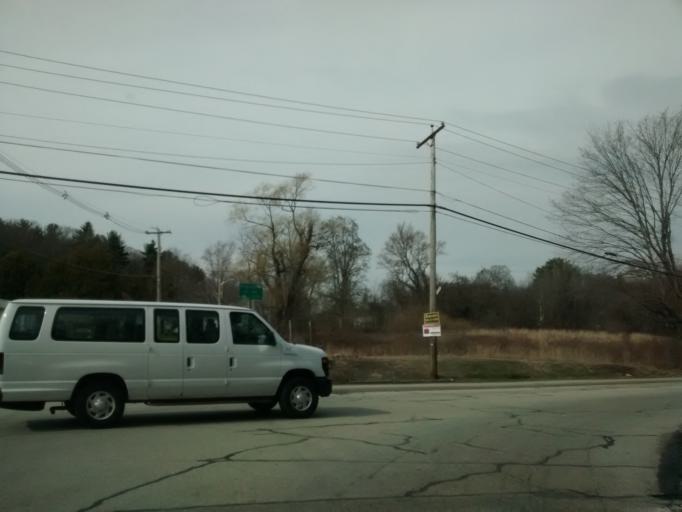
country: US
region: Massachusetts
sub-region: Worcester County
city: East Douglas
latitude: 42.0780
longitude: -71.7090
